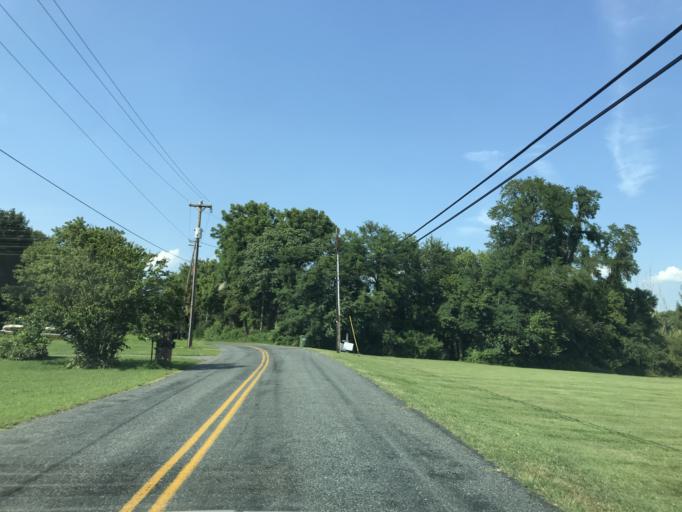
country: US
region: Maryland
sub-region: Harford County
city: South Bel Air
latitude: 39.6281
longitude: -76.2748
